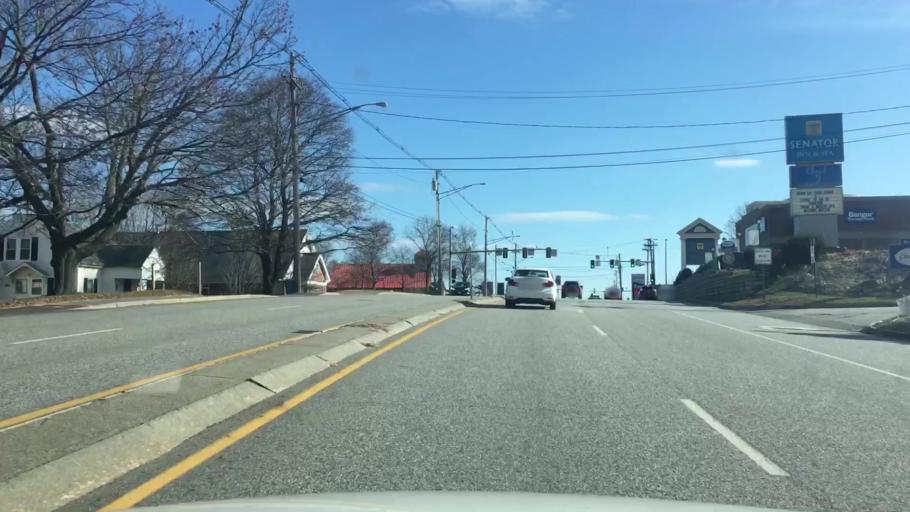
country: US
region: Maine
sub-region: Kennebec County
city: Augusta
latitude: 44.3159
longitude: -69.8066
